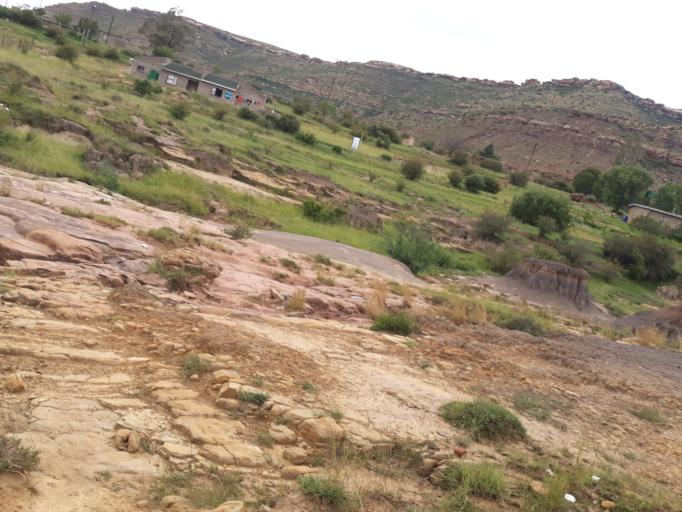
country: LS
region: Quthing
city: Quthing
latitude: -30.3377
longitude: 27.5331
